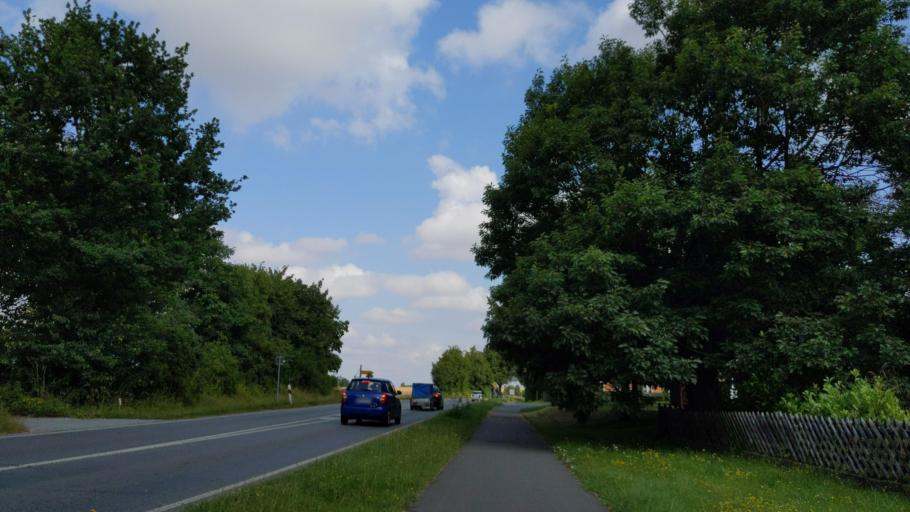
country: DE
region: Schleswig-Holstein
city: Stockelsdorf
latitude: 53.9265
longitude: 10.6372
